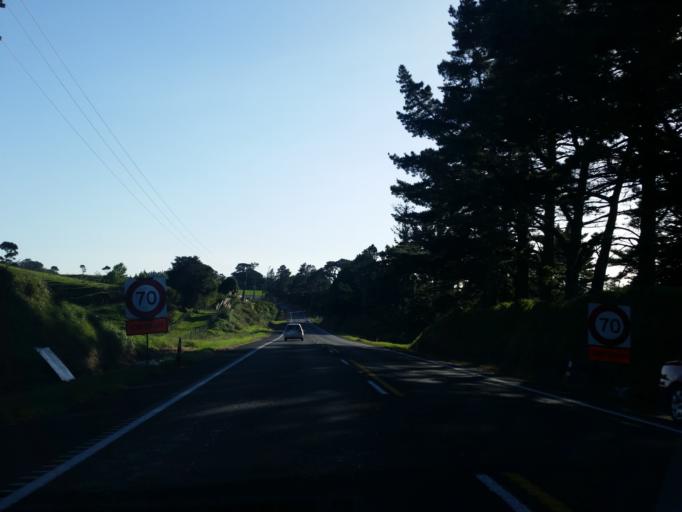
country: NZ
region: Bay of Plenty
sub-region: Western Bay of Plenty District
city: Waihi Beach
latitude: -37.4689
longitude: 175.9359
